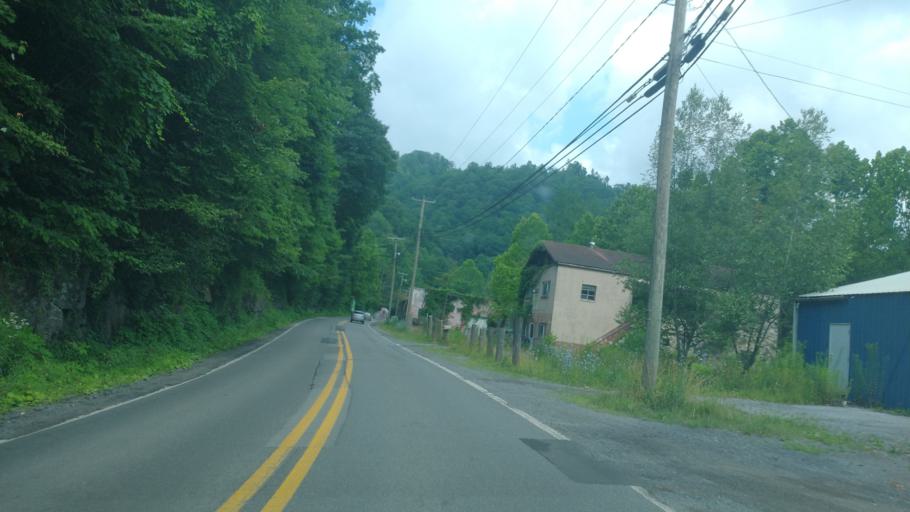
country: US
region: West Virginia
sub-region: McDowell County
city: Welch
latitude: 37.4051
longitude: -81.4219
